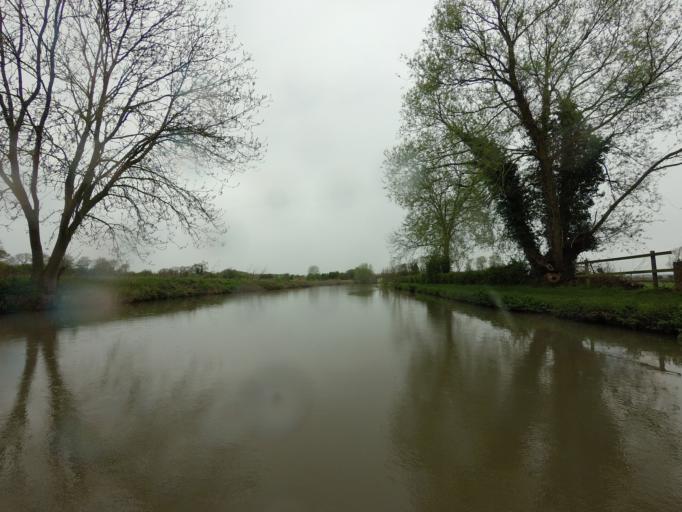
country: GB
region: England
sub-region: Milton Keynes
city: Castlethorpe
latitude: 52.1036
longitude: -0.8851
